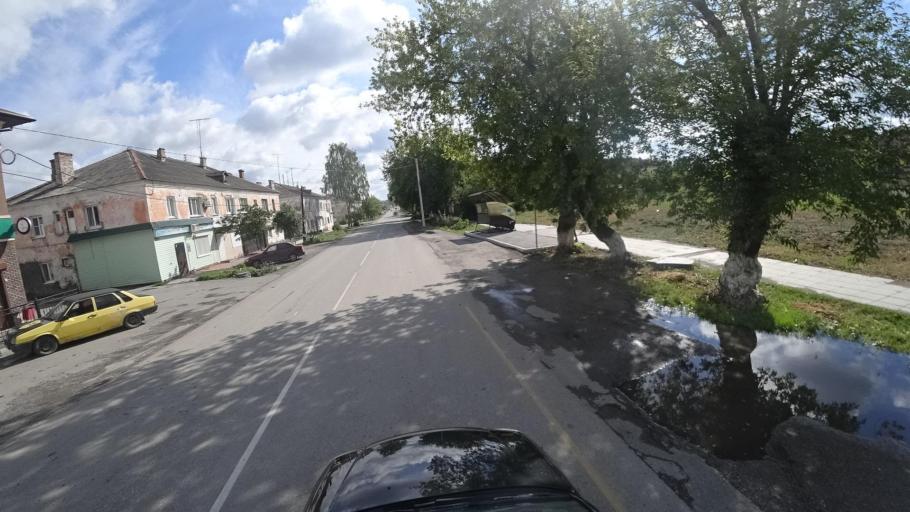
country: RU
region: Sverdlovsk
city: Kamyshlov
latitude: 56.8465
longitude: 62.7119
